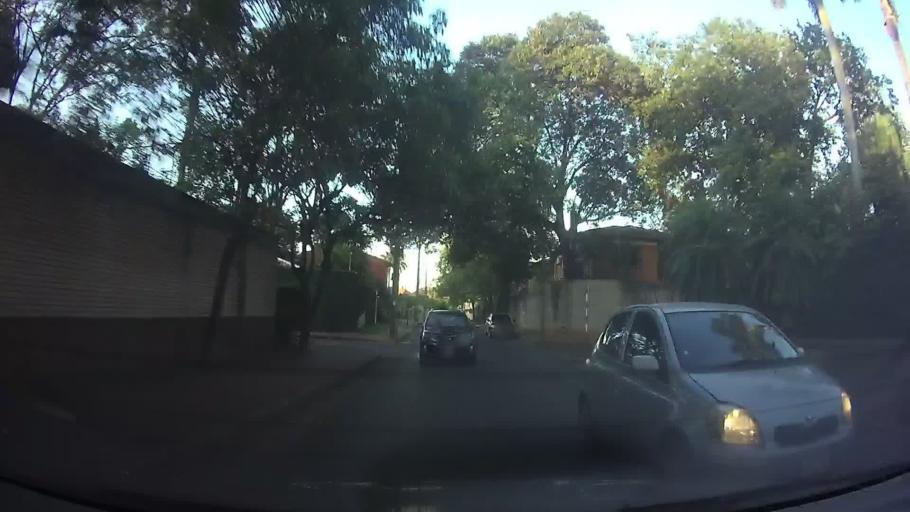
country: PY
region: Central
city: Lambare
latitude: -25.3015
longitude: -57.5749
